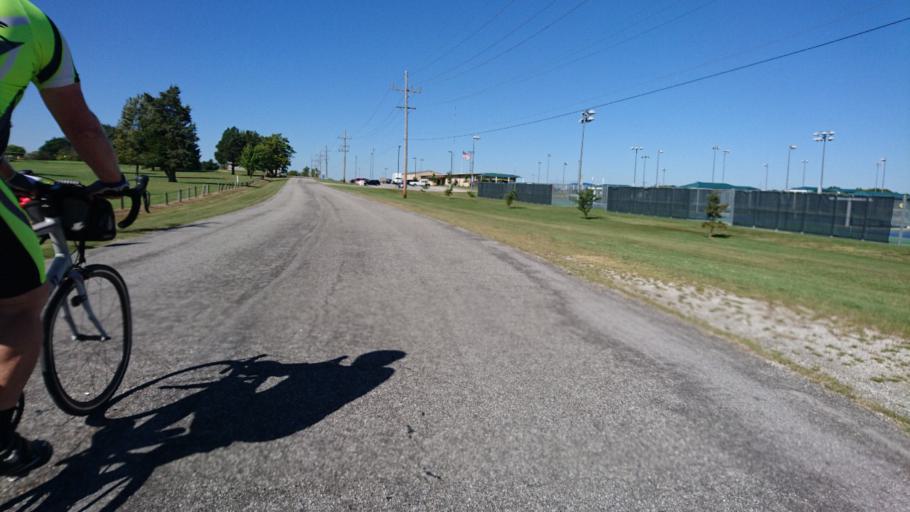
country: US
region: Missouri
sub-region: Jasper County
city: Joplin
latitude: 37.0919
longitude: -94.5533
